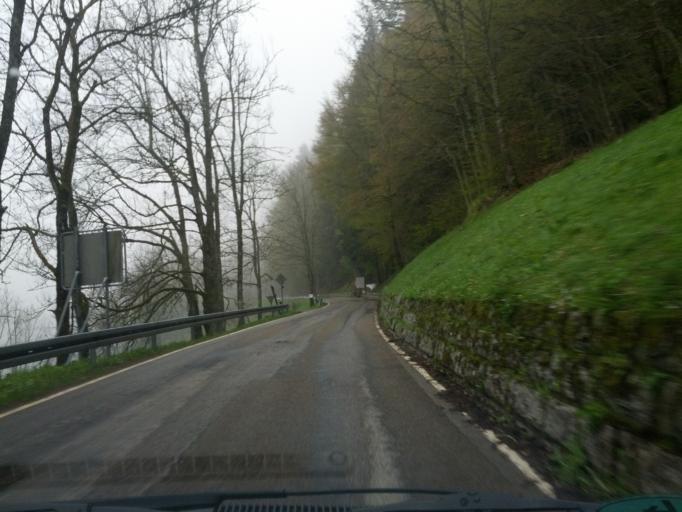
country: DE
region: Baden-Wuerttemberg
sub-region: Freiburg Region
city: Bollen
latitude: 47.7946
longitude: 7.8263
